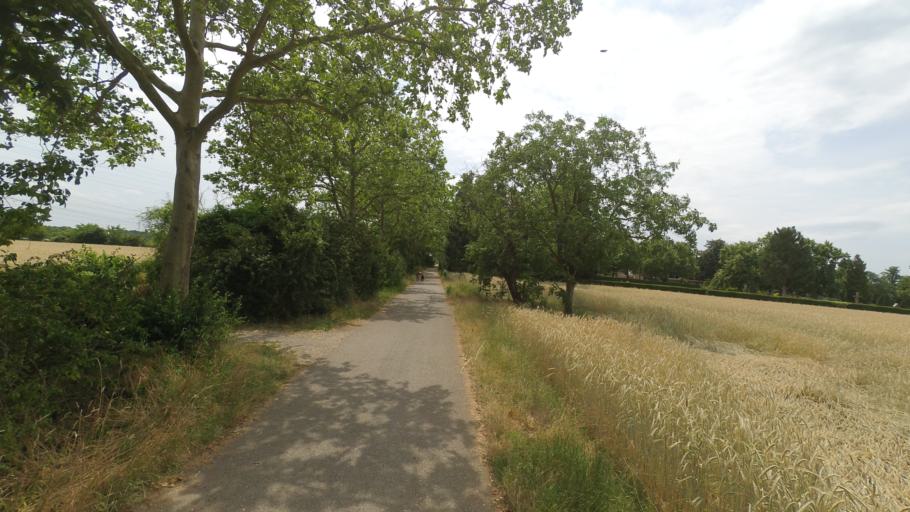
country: DE
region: Baden-Wuerttemberg
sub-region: Karlsruhe Region
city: Bruhl
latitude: 49.3890
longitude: 8.5386
